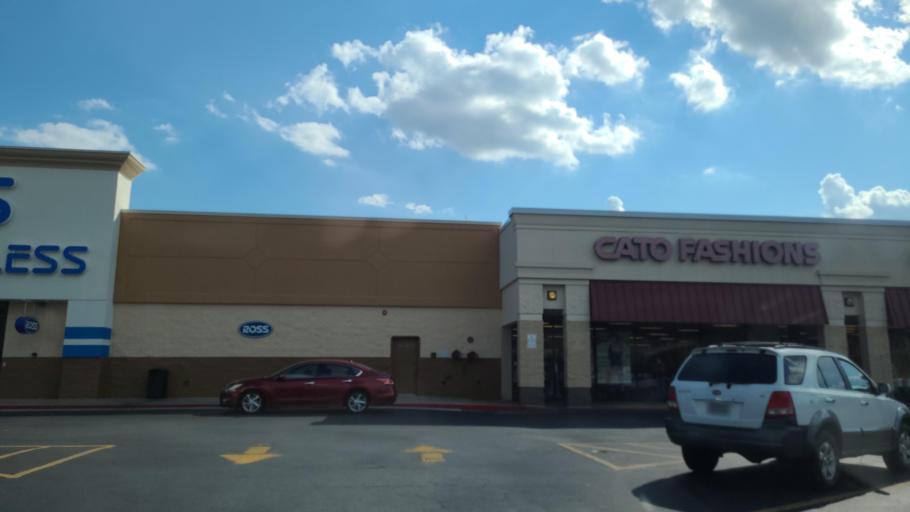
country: US
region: Georgia
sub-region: Gordon County
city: Calhoun
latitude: 34.4744
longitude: -84.9289
